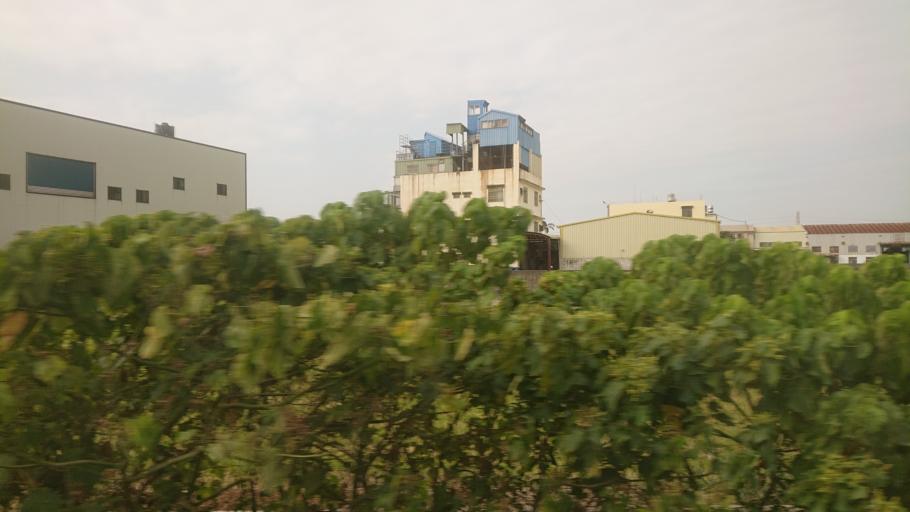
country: TW
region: Taiwan
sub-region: Changhua
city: Chang-hua
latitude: 24.0290
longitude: 120.5353
